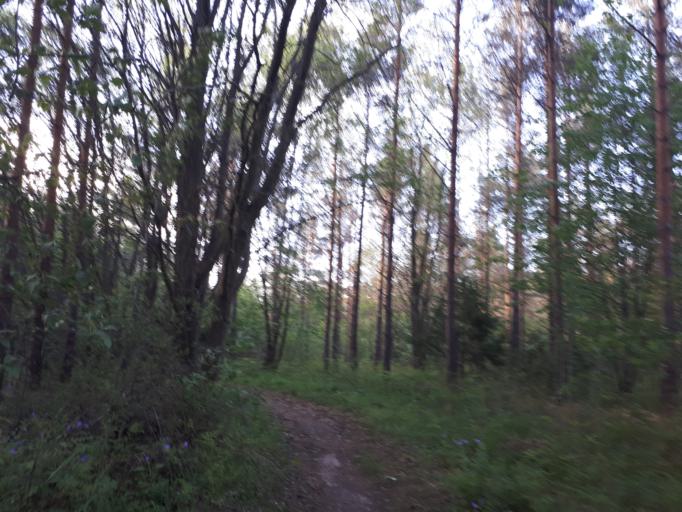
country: SE
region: Gotland
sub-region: Gotland
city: Visby
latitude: 57.6021
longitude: 18.3012
